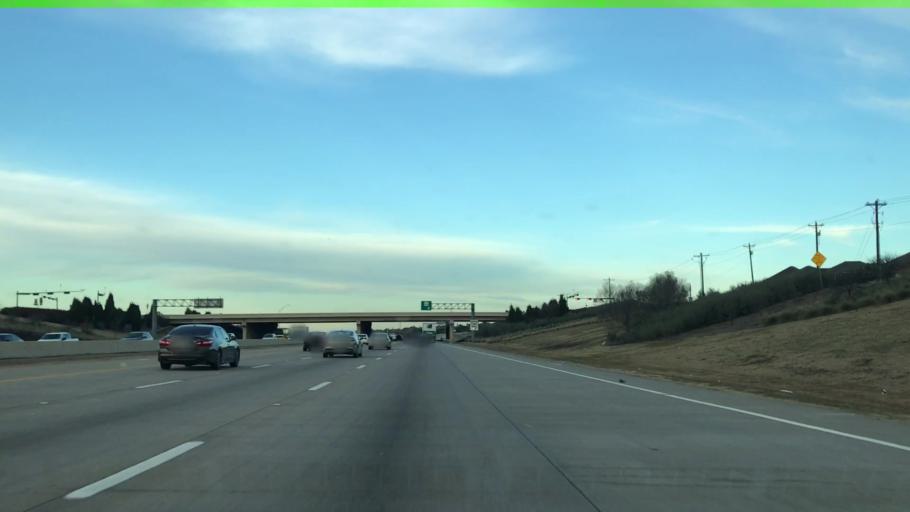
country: US
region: Texas
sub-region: Denton County
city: The Colony
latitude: 33.0337
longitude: -96.9259
